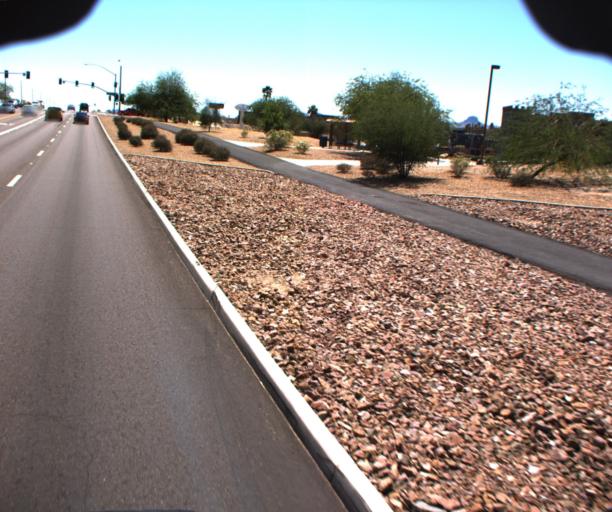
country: US
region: Arizona
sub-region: Mohave County
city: Lake Havasu City
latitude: 34.4730
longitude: -114.3449
